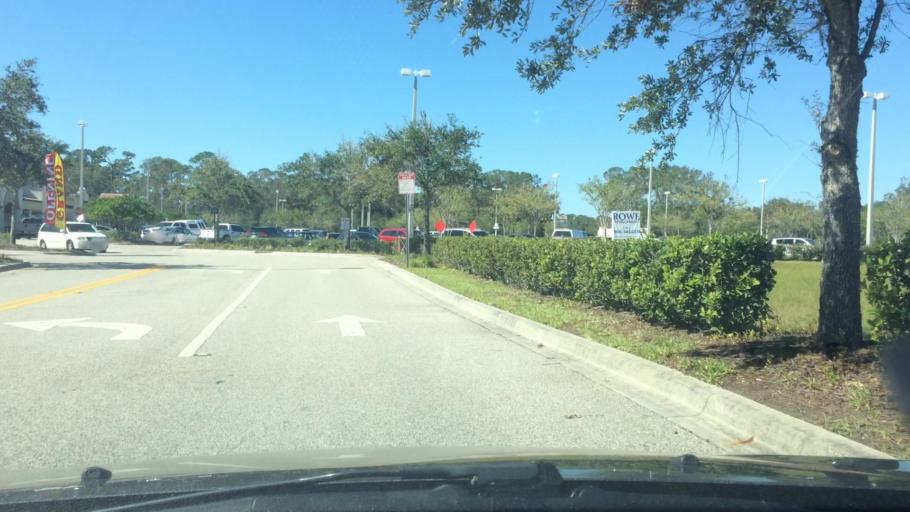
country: US
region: Florida
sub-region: Saint Johns County
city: Saint Augustine
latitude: 29.9153
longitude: -81.3612
